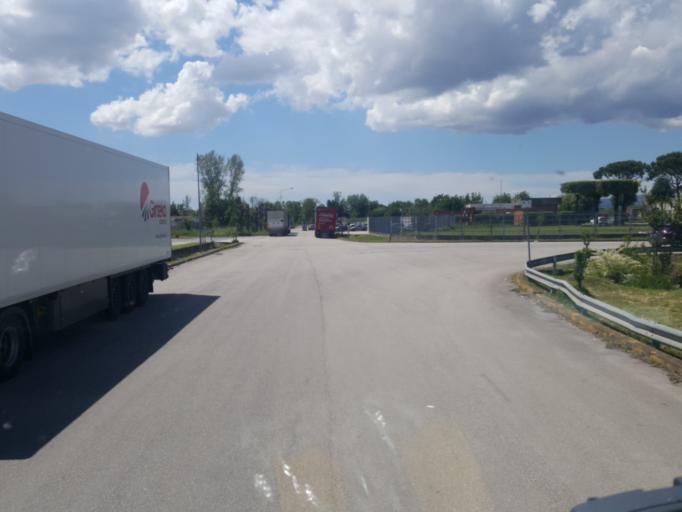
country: IT
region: Campania
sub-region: Provincia di Napoli
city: Pascarola
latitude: 40.9820
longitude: 14.3010
